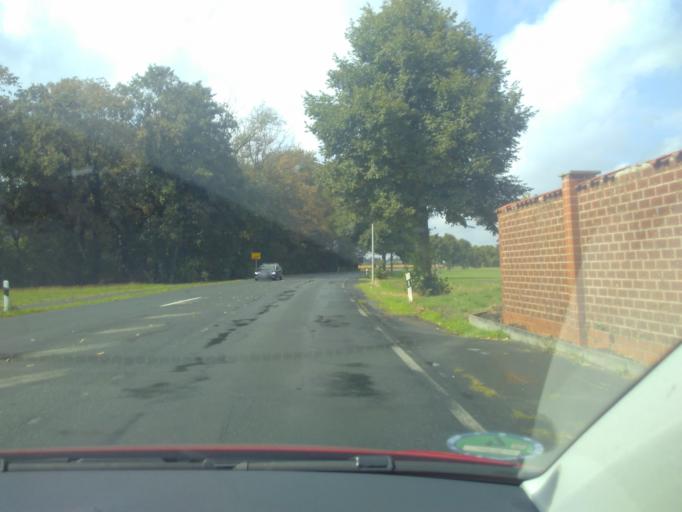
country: DE
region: North Rhine-Westphalia
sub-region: Regierungsbezirk Munster
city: Warendorf
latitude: 52.0004
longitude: 7.9389
